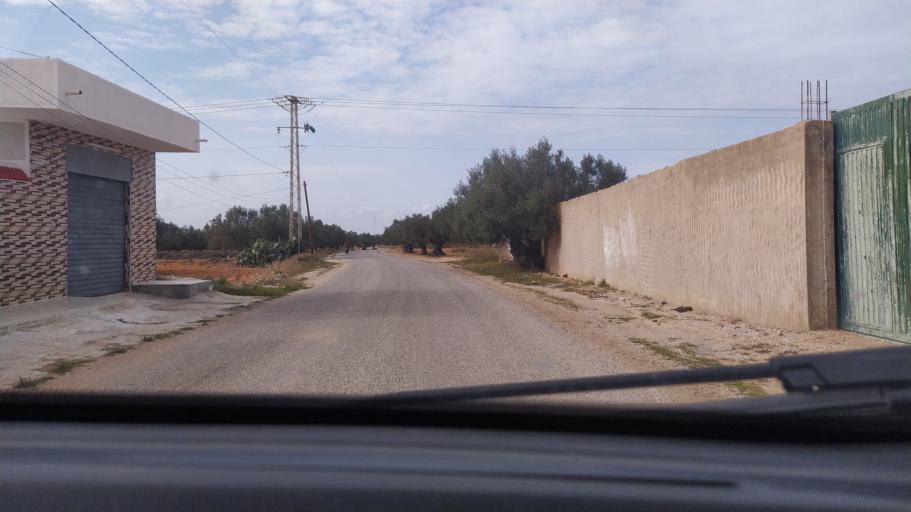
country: TN
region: Al Munastir
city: Sidi Bin Nur
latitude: 35.5244
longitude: 10.9695
